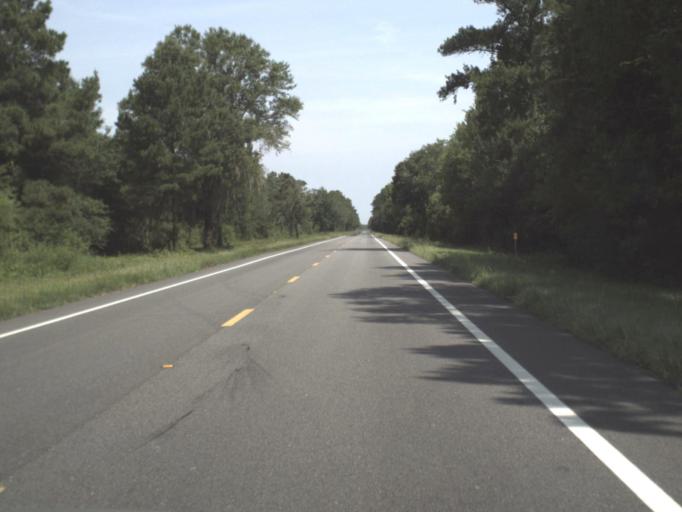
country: US
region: Florida
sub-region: Hamilton County
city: Jasper
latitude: 30.5858
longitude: -83.0027
